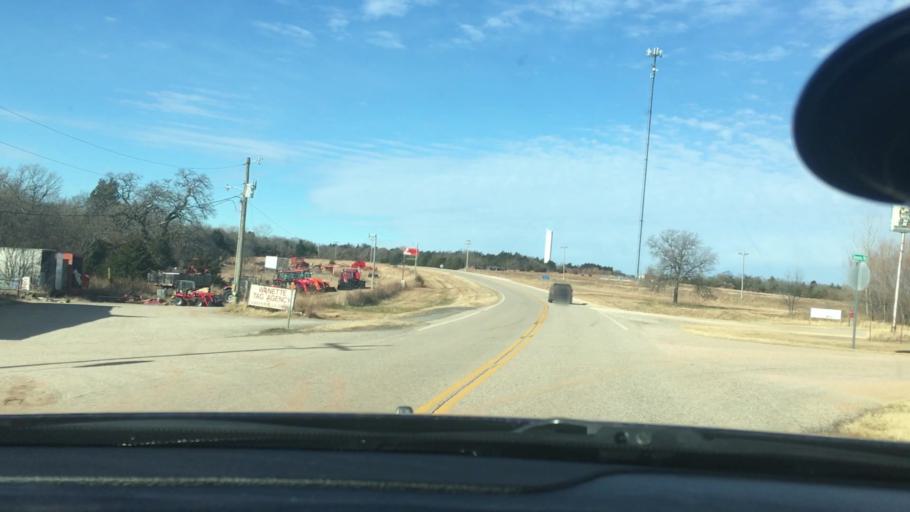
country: US
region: Oklahoma
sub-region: Garvin County
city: Stratford
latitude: 35.0138
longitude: -97.0714
